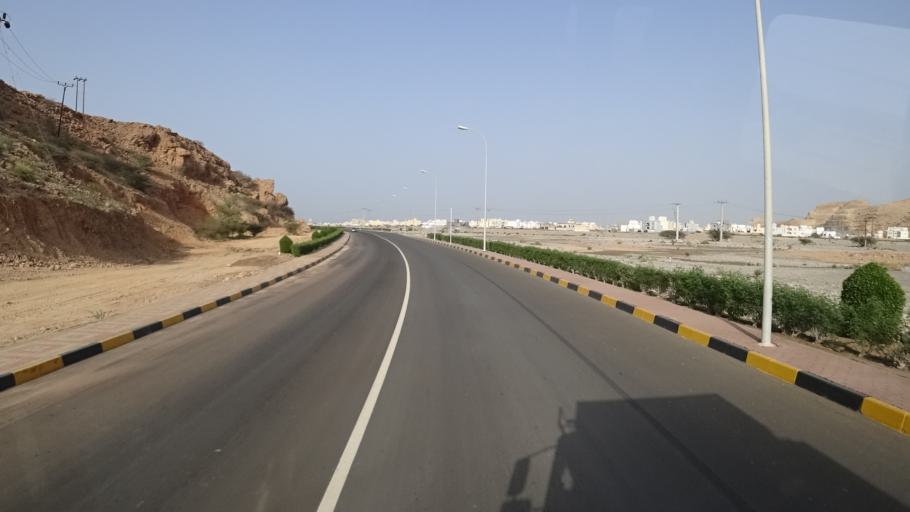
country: OM
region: Muhafazat Masqat
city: Muscat
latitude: 23.2124
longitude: 58.8817
